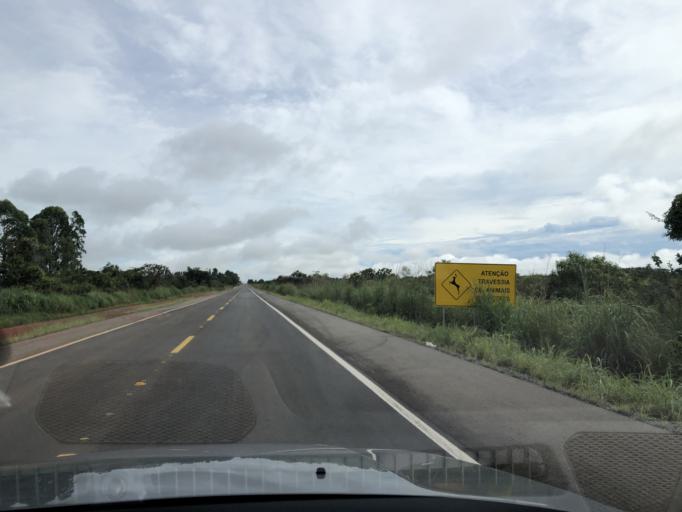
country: BR
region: Federal District
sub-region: Brasilia
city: Brasilia
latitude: -15.6554
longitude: -48.0832
